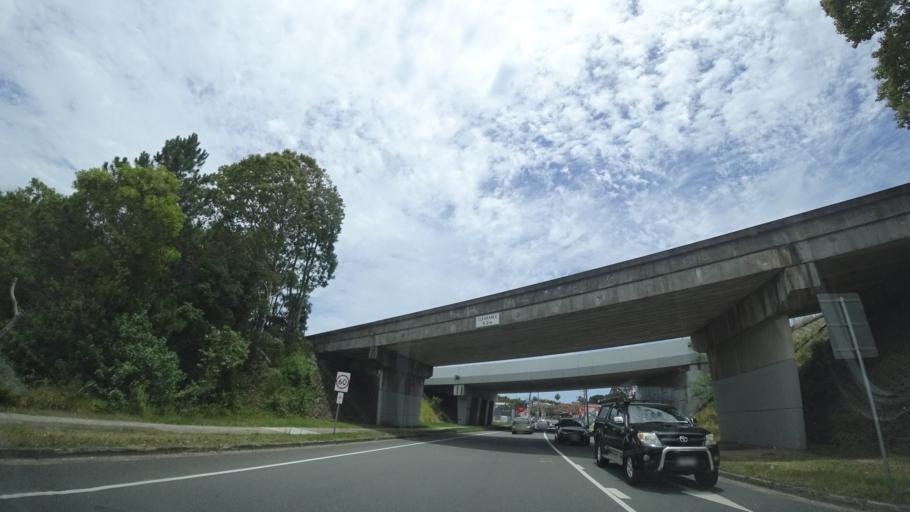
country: AU
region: Queensland
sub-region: Sunshine Coast
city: Mooloolaba
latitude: -26.6731
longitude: 153.0948
